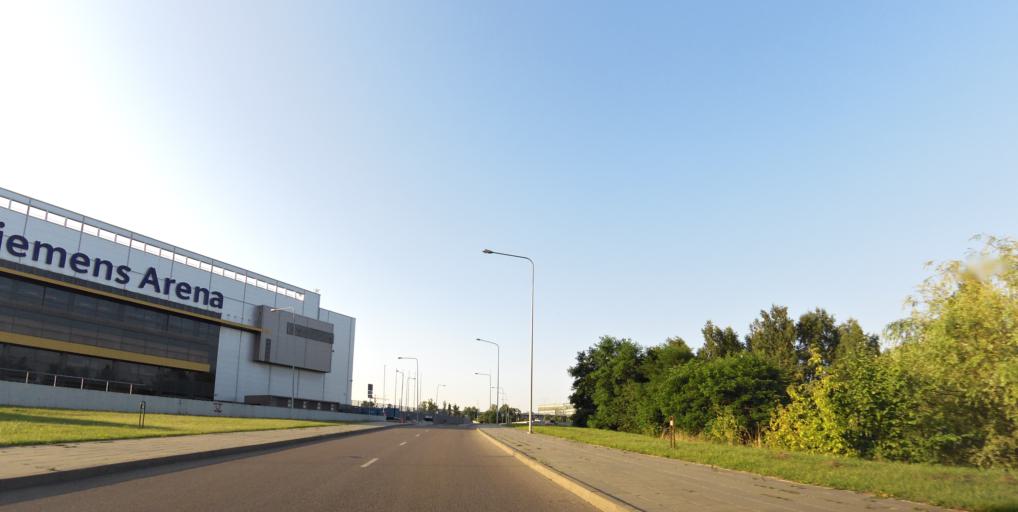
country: LT
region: Vilnius County
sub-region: Vilnius
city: Vilnius
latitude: 54.7152
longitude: 25.2808
